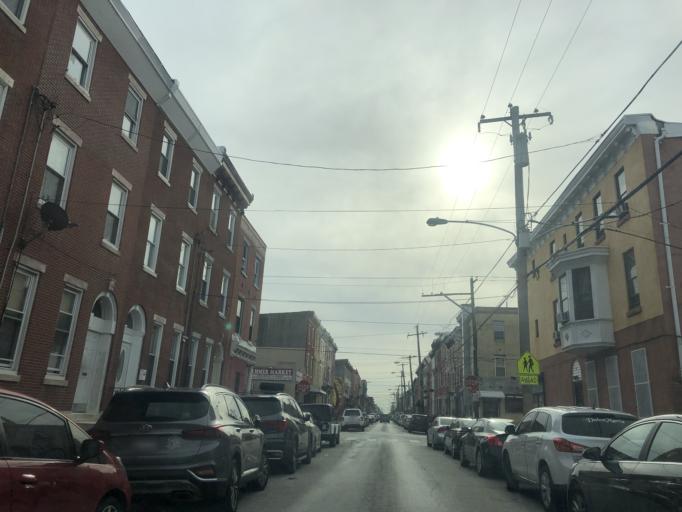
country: US
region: Pennsylvania
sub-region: Philadelphia County
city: Philadelphia
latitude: 39.9304
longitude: -75.1549
